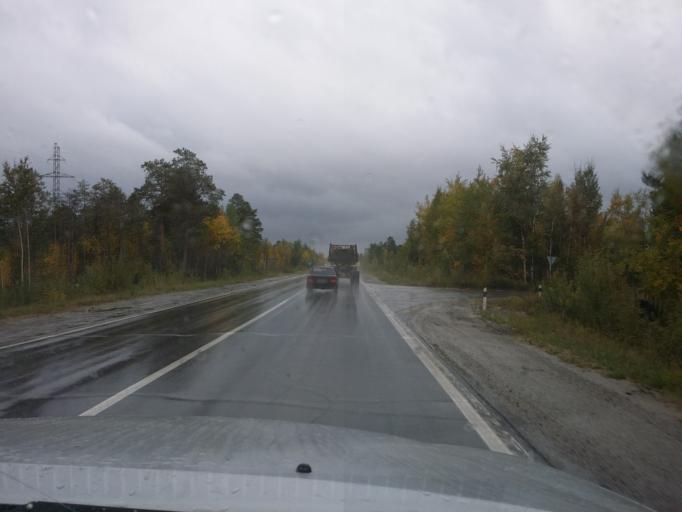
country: RU
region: Khanty-Mansiyskiy Avtonomnyy Okrug
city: Megion
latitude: 61.1383
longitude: 75.7631
